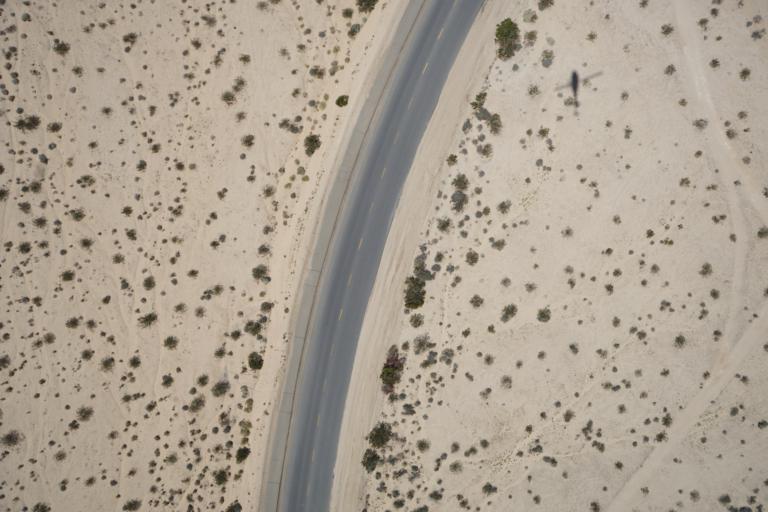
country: US
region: California
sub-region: San Bernardino County
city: Twentynine Palms
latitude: 34.1403
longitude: -116.0628
